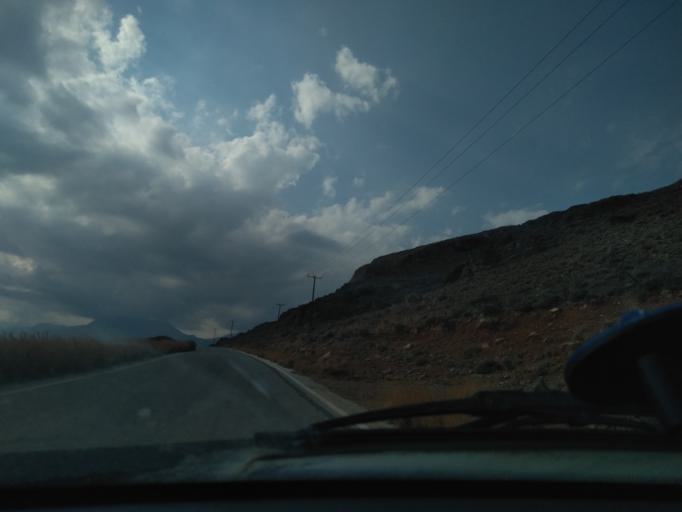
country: GR
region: Crete
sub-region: Nomos Lasithiou
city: Makry-Gialos
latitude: 35.0188
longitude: 26.0228
